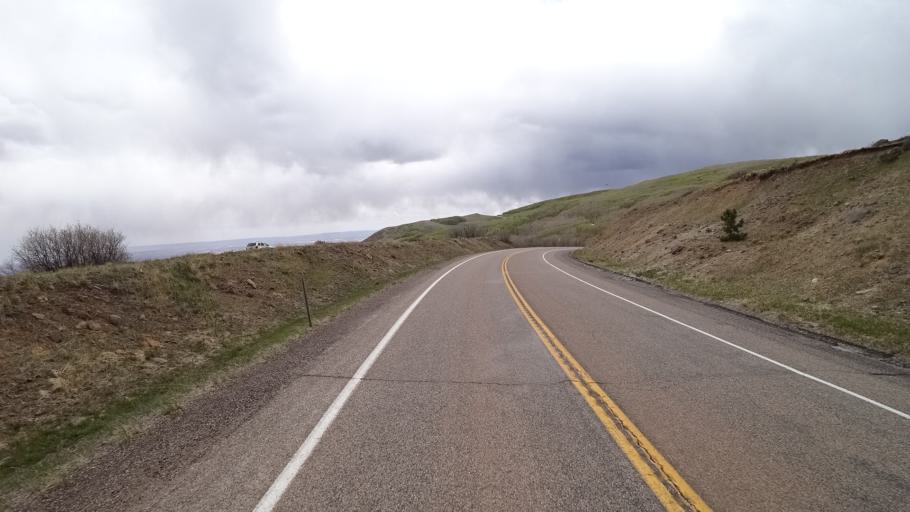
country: US
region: Utah
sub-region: Wayne County
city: Loa
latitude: 38.0275
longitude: -111.3433
